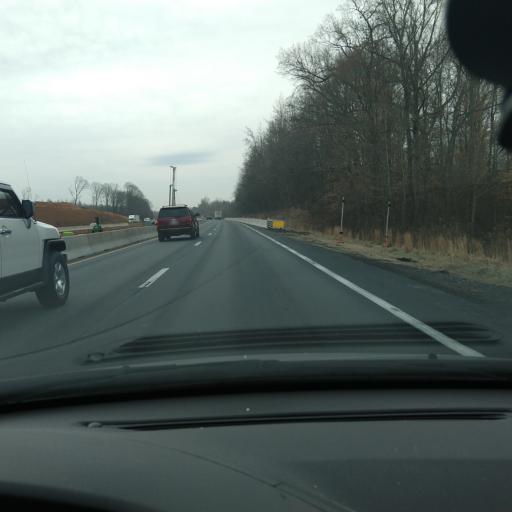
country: US
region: North Carolina
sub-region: Rowan County
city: China Grove
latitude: 35.5365
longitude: -80.5740
